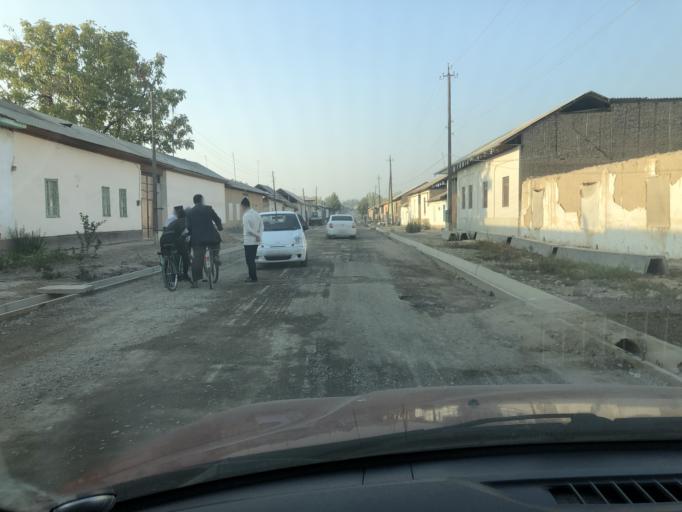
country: UZ
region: Namangan
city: Uychi
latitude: 41.0776
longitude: 72.0020
